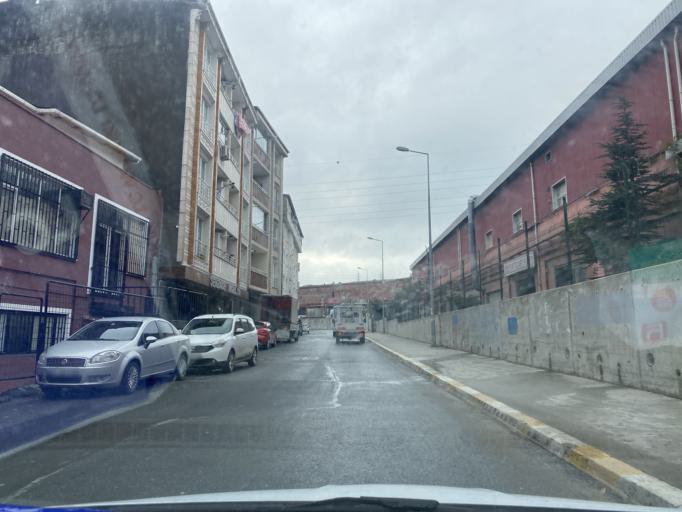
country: TR
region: Istanbul
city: Esenyurt
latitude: 41.0183
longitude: 28.6940
